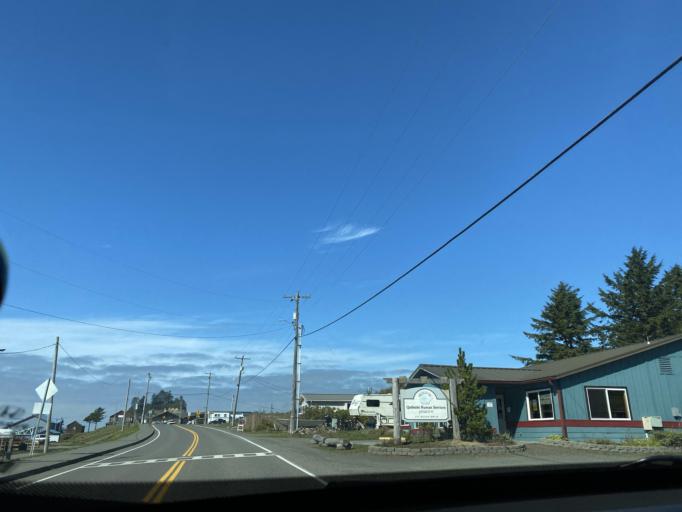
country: US
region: Washington
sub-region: Clallam County
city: Forks
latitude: 47.9072
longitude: -124.6341
